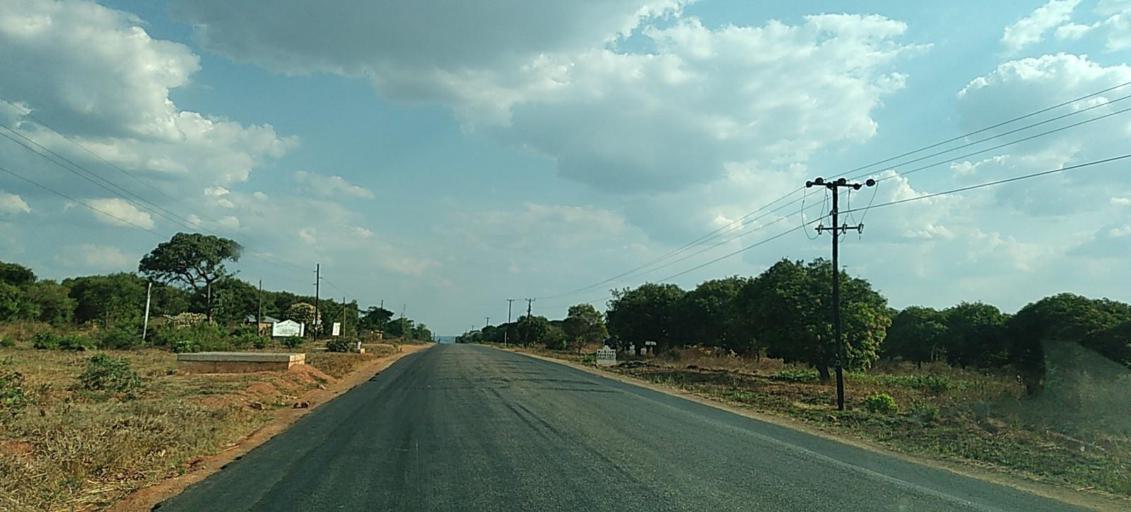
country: ZM
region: Copperbelt
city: Luanshya
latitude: -13.3142
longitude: 28.4139
